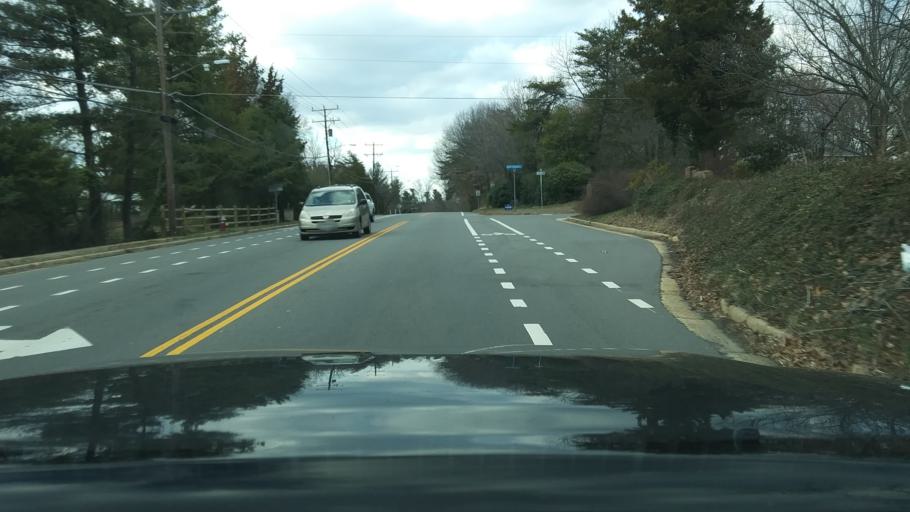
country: US
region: Virginia
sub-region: Fairfax County
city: Lake Barcroft
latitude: 38.8382
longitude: -77.1714
